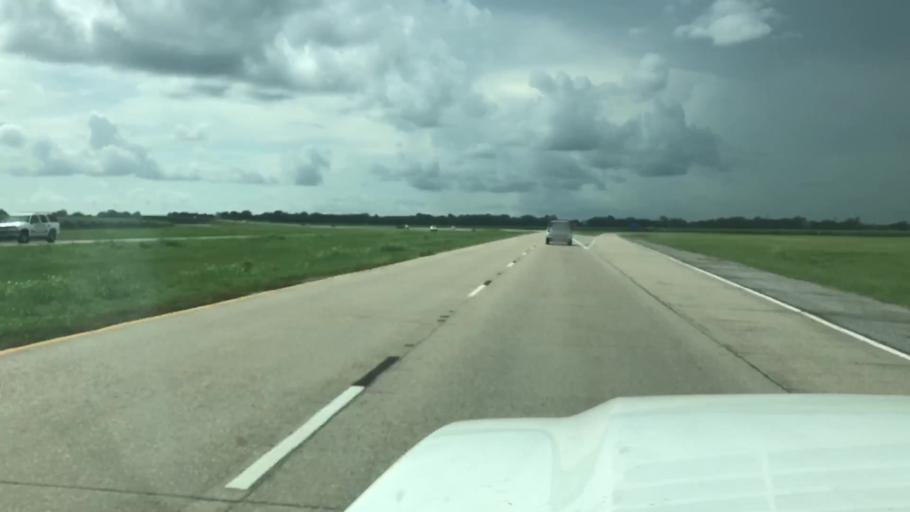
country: US
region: Louisiana
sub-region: Saint Mary Parish
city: Franklin
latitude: 29.7559
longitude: -91.4542
